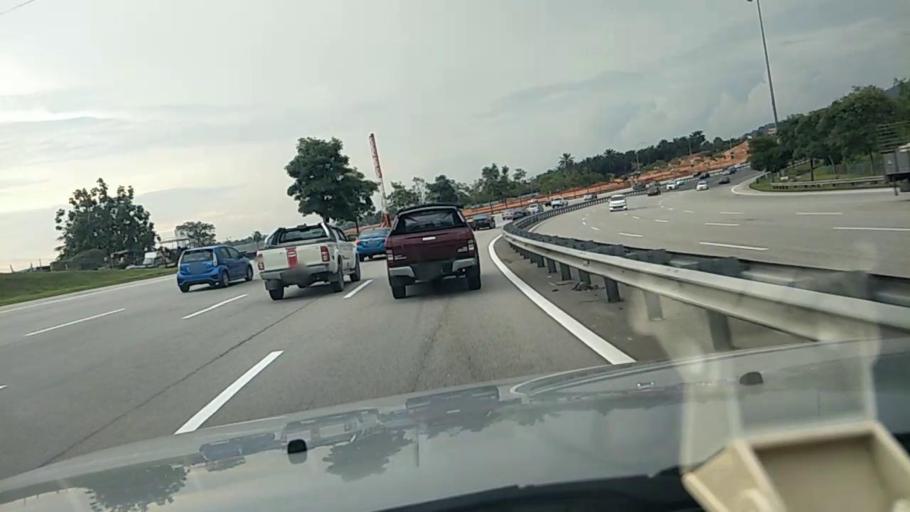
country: MY
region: Selangor
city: Shah Alam
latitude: 3.0928
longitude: 101.4828
